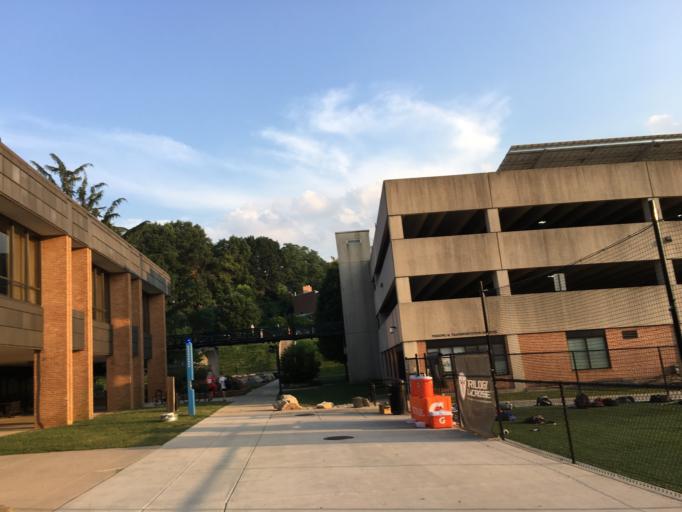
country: US
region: Maryland
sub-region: Baltimore County
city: Towson
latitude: 39.3935
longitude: -76.6117
